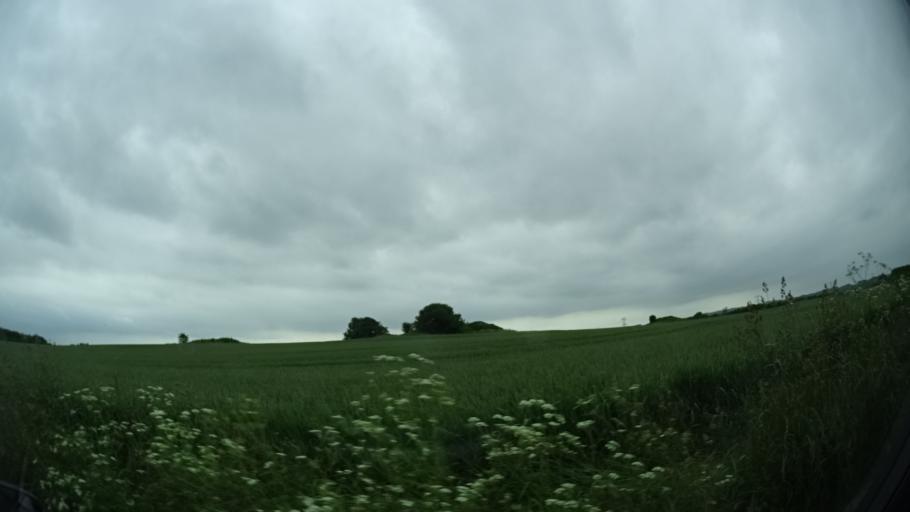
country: DK
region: Central Jutland
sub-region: Arhus Kommune
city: Kolt
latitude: 56.0969
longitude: 10.0697
